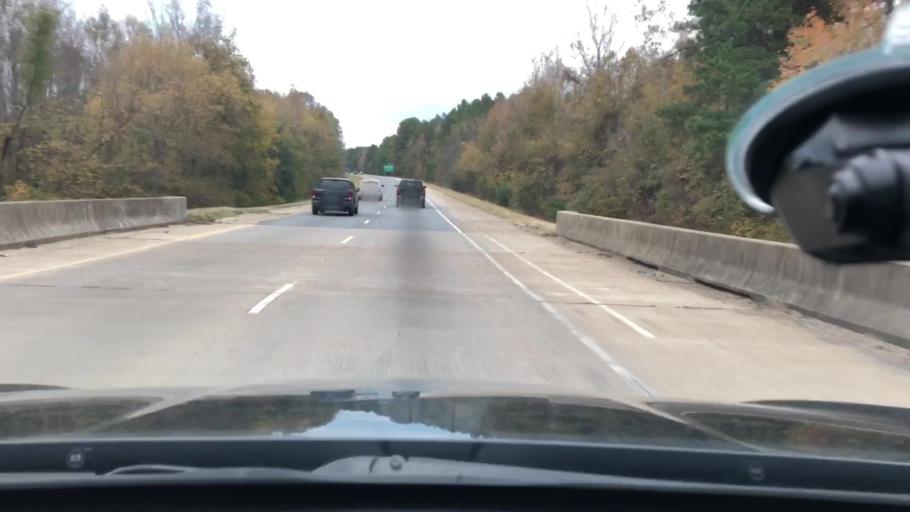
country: US
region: Arkansas
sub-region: Clark County
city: Arkadelphia
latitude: 34.0982
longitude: -93.1040
